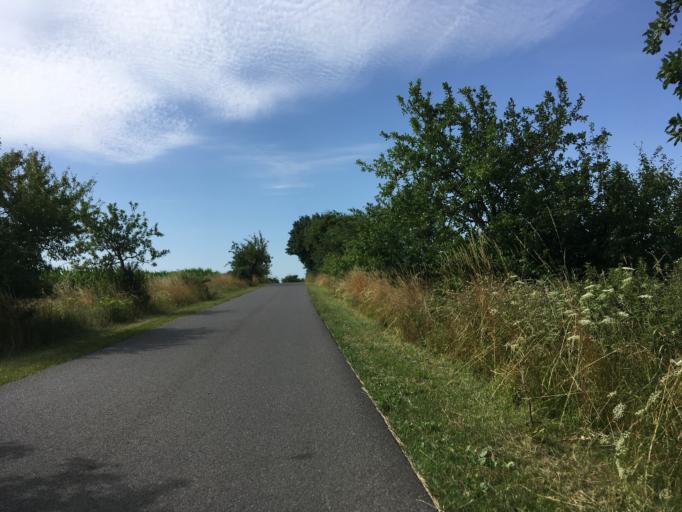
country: DE
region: Brandenburg
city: Zichow
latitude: 53.2055
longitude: 14.0448
